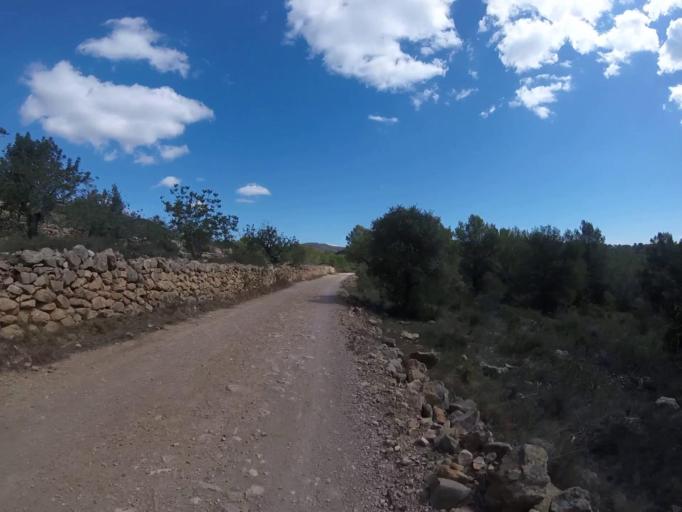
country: ES
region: Valencia
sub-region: Provincia de Castello
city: Santa Magdalena de Pulpis
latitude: 40.3144
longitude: 0.3299
